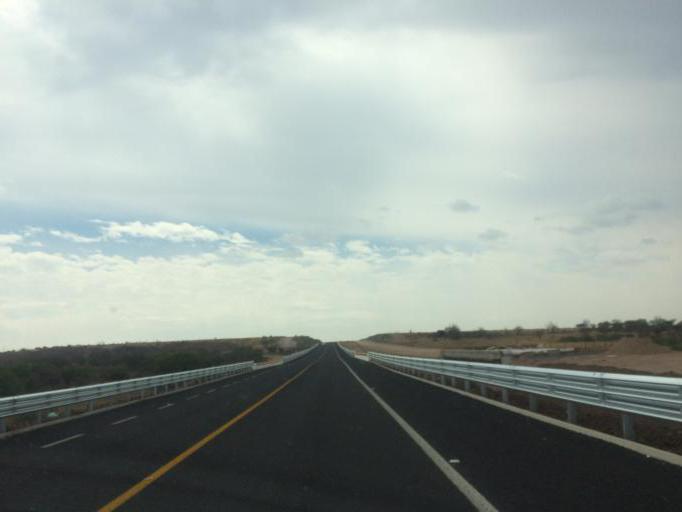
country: MX
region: Guanajuato
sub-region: Leon
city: Ladrilleras del Refugio
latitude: 21.0713
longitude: -101.5396
